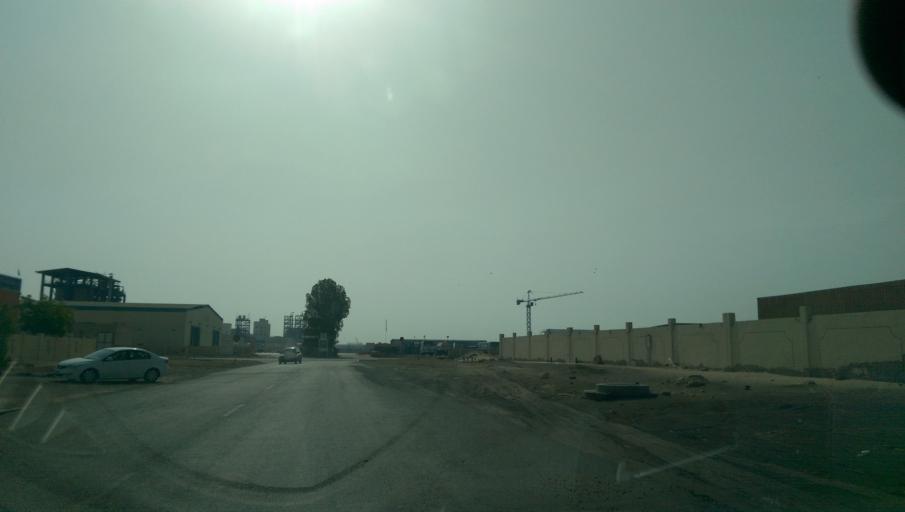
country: AE
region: Abu Dhabi
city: Abu Dhabi
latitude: 24.3246
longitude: 54.4832
